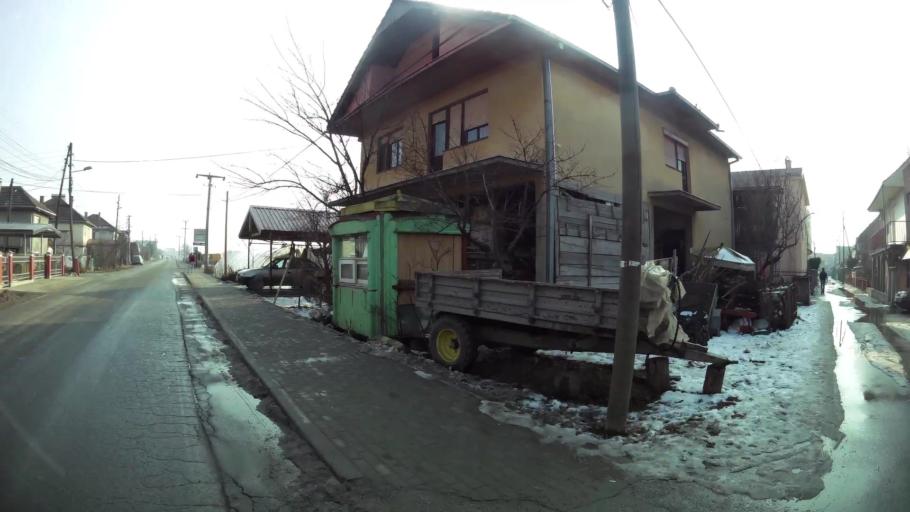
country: MK
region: Ilinden
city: Marino
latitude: 41.9890
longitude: 21.5871
